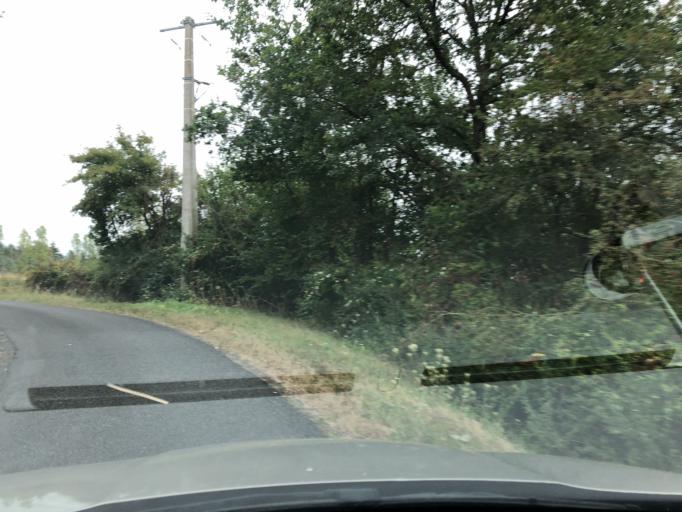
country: FR
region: Centre
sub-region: Departement d'Indre-et-Loire
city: Villandry
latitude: 47.3652
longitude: 0.4939
